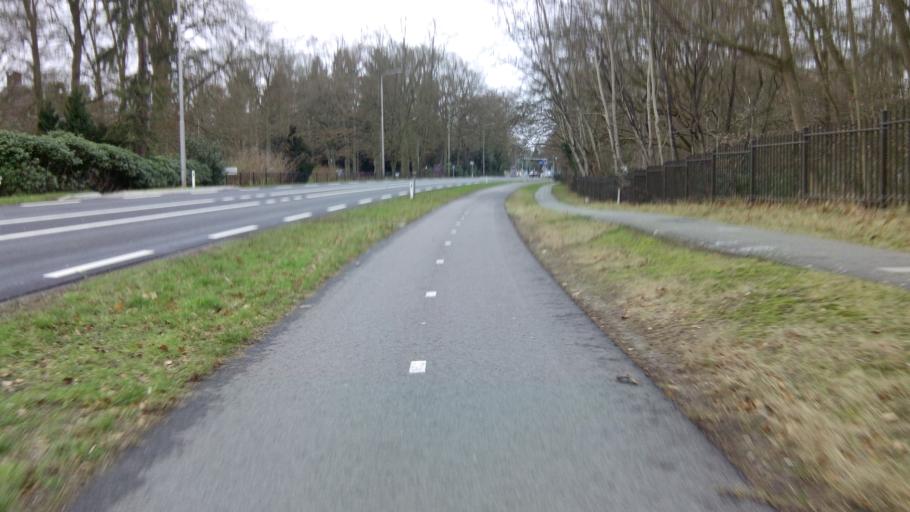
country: NL
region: North Holland
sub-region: Gemeente Hilversum
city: Hilversum
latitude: 52.2108
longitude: 5.2038
